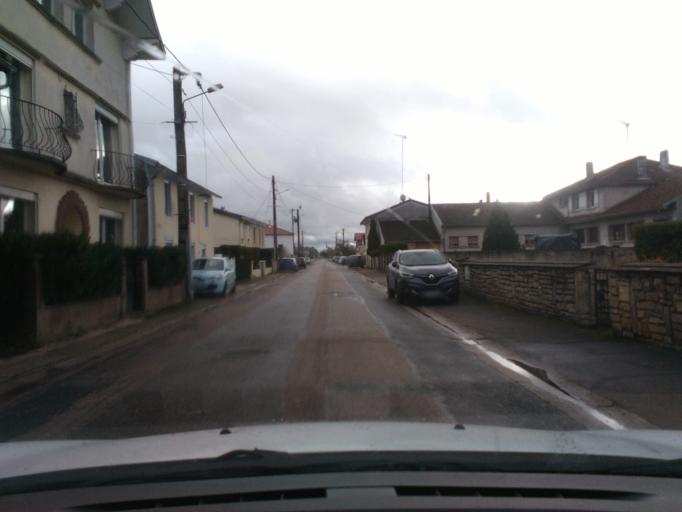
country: FR
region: Lorraine
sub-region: Departement des Vosges
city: Charmes
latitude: 48.3947
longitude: 6.2539
